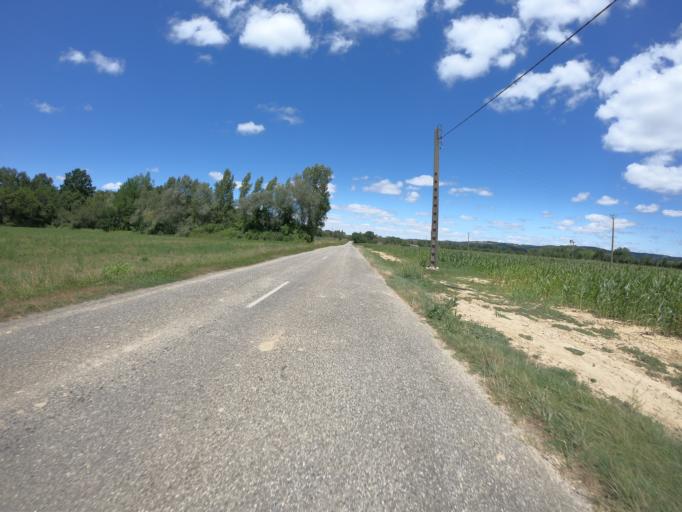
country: FR
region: Midi-Pyrenees
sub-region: Departement de l'Ariege
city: Verniolle
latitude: 43.0728
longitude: 1.7389
